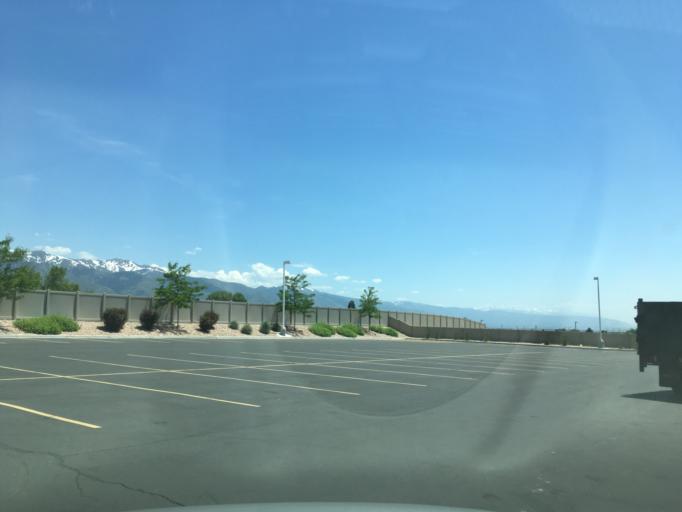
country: US
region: Utah
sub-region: Davis County
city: Hill Air Force Bace
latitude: 41.1006
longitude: -111.9812
